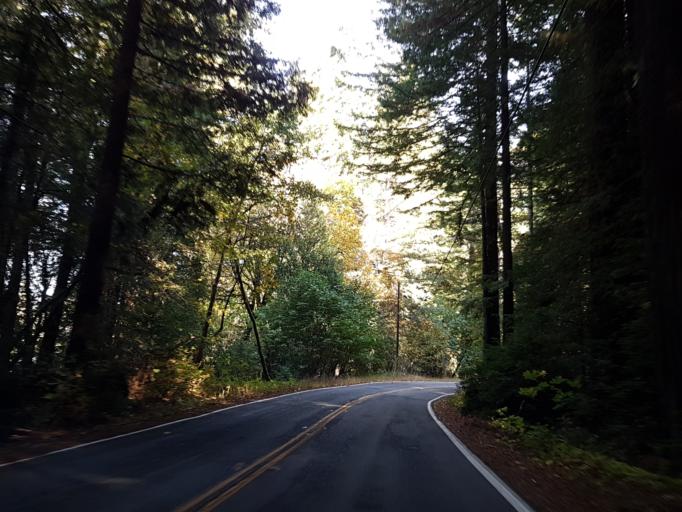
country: US
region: California
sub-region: Humboldt County
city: Rio Dell
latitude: 40.4163
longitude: -123.9642
